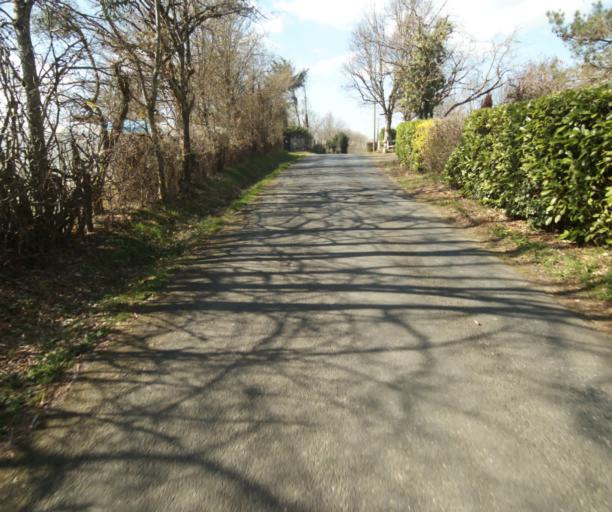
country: FR
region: Limousin
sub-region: Departement de la Correze
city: Saint-Mexant
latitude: 45.3058
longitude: 1.6539
